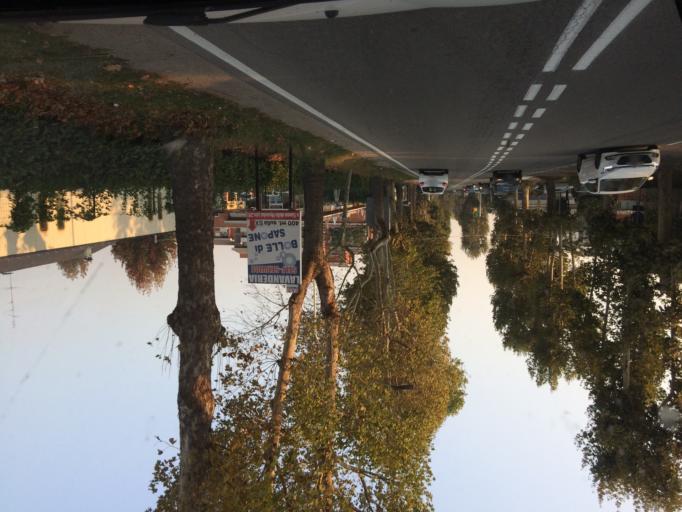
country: IT
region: Lombardy
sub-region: Provincia di Varese
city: Castellanza
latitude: 45.6078
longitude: 8.8901
